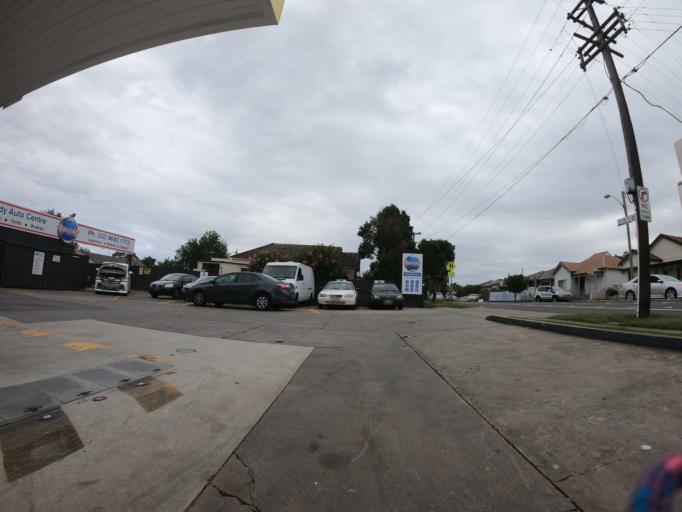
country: AU
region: New South Wales
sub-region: Parramatta
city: Granville
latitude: -33.8474
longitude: 151.0128
